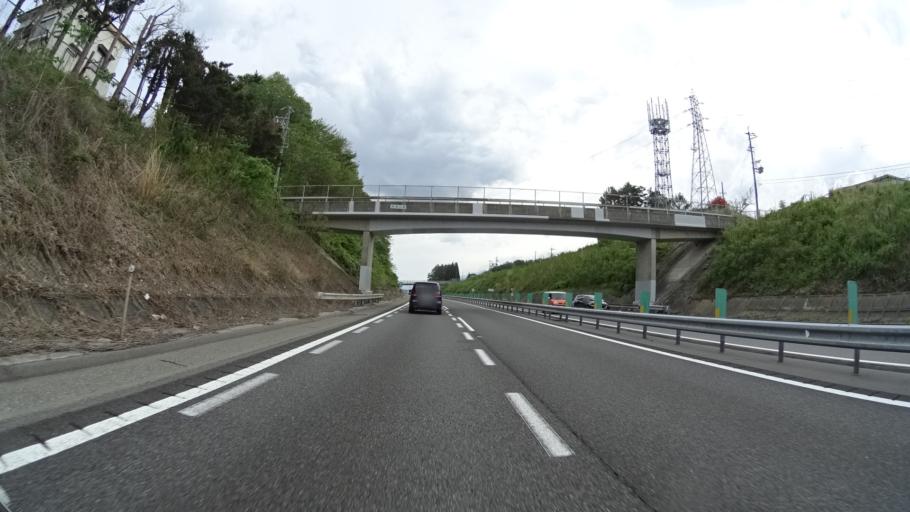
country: JP
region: Nagano
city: Tatsuno
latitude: 35.9695
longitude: 137.9972
